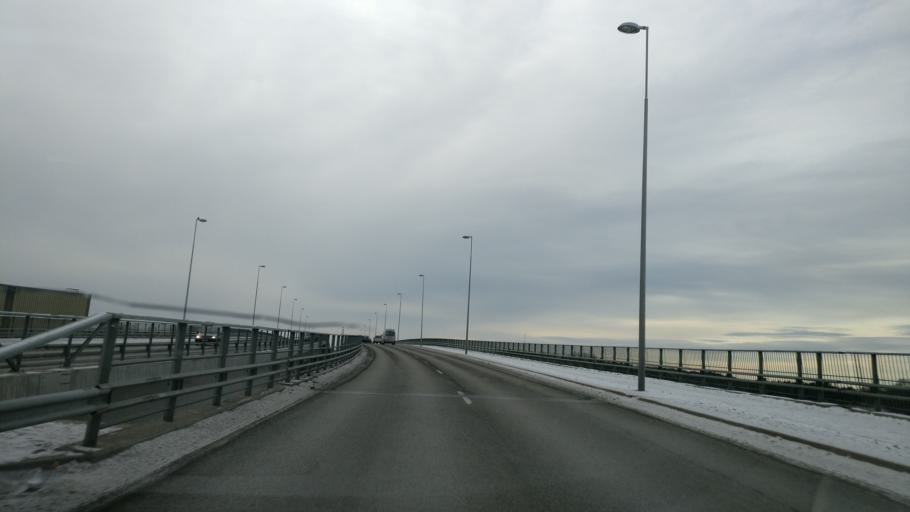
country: FI
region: Southern Savonia
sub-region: Savonlinna
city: Savonlinna
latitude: 61.8705
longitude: 28.9126
